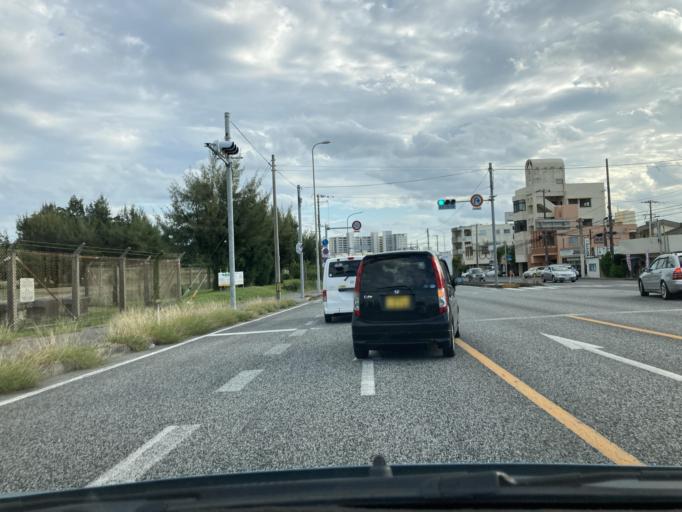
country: JP
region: Okinawa
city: Chatan
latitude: 26.3311
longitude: 127.7518
